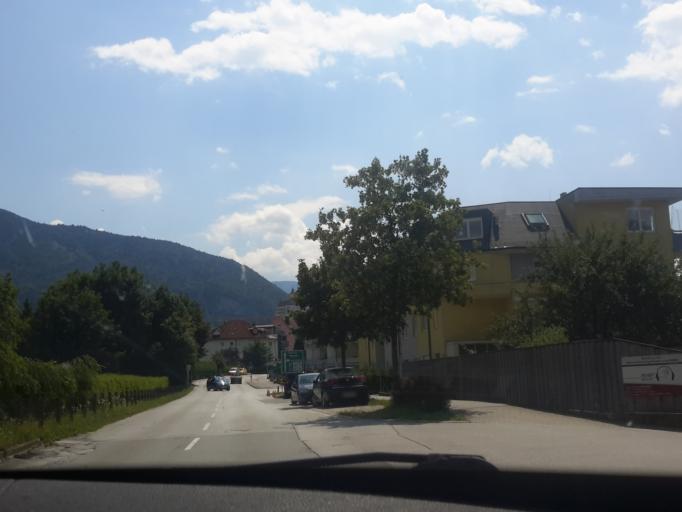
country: AT
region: Tyrol
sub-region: Politischer Bezirk Kufstein
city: Kufstein
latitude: 47.5895
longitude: 12.1710
